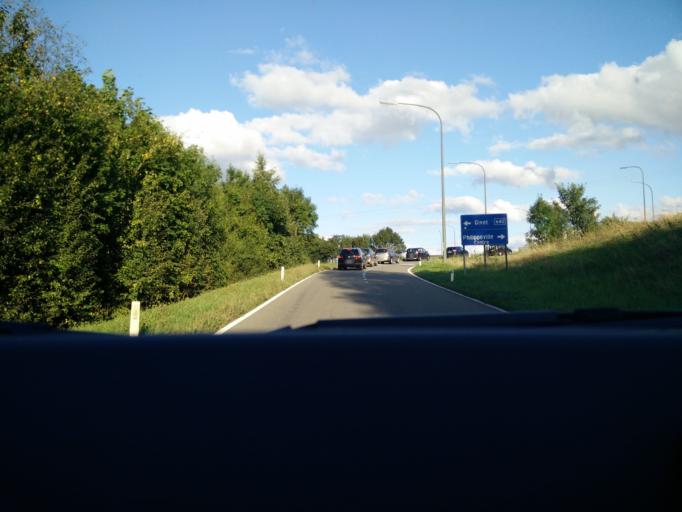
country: BE
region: Wallonia
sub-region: Province de Namur
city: Philippeville
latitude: 50.2006
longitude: 4.5528
